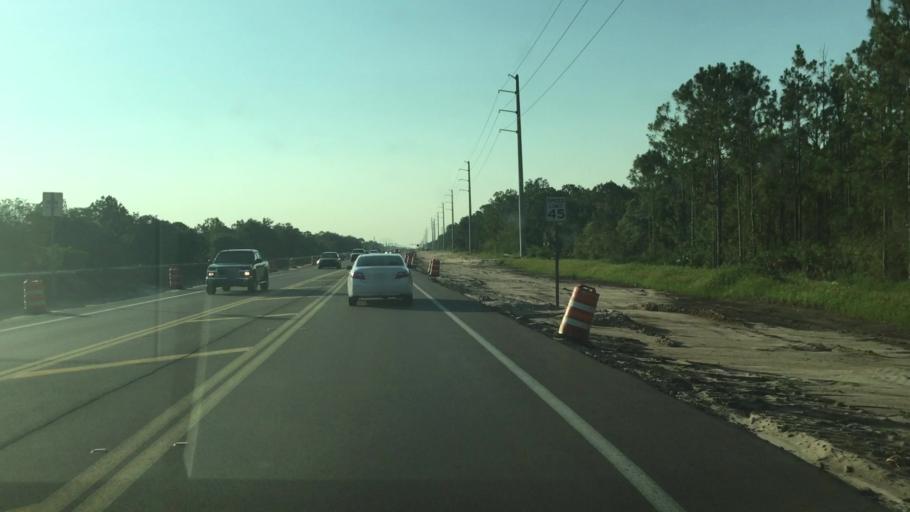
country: US
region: Florida
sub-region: Lee County
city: Gateway
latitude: 26.5860
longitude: -81.7239
